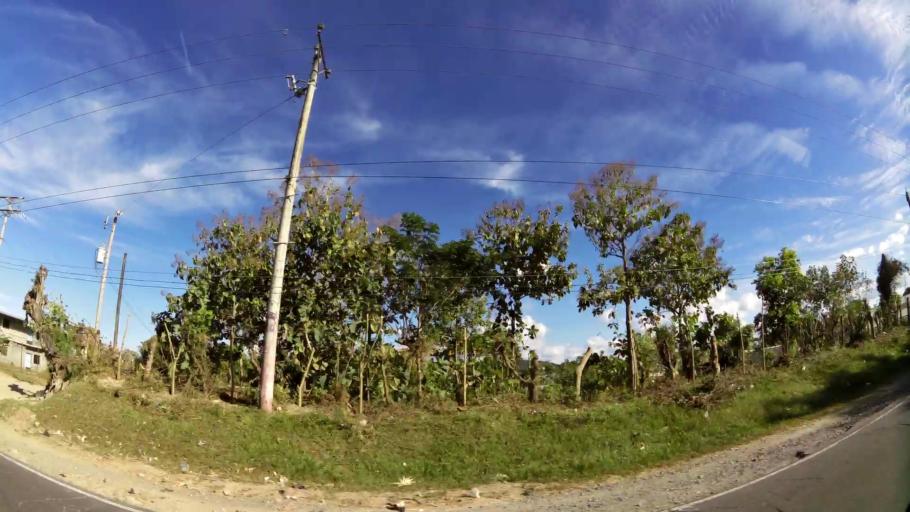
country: SV
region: Cuscatlan
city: Tecoluca
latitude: 13.7906
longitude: -89.0447
